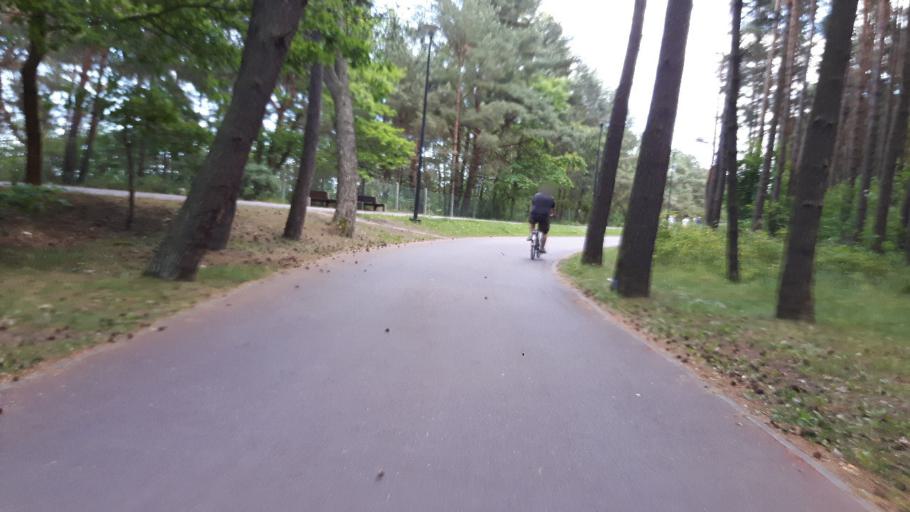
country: PL
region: Pomeranian Voivodeship
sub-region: Sopot
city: Sopot
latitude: 54.4187
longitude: 18.6105
